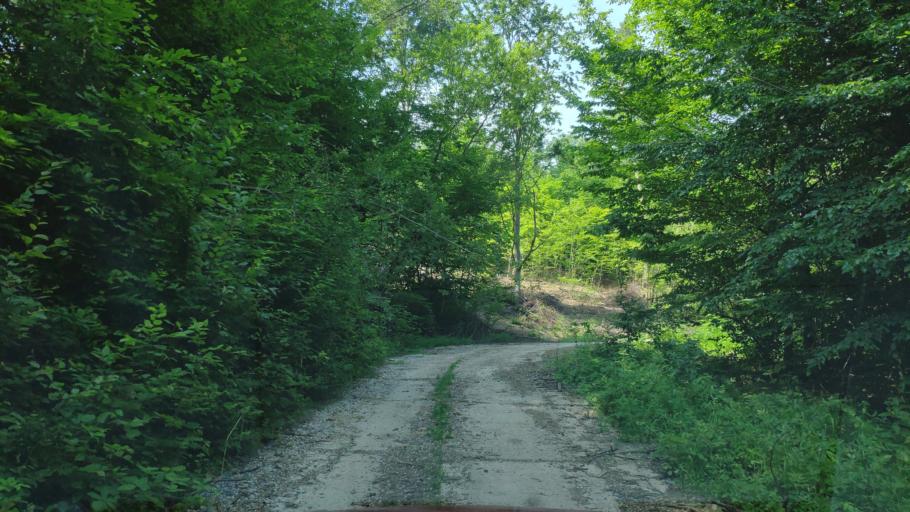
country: SK
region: Presovsky
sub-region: Okres Presov
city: Presov
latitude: 48.9720
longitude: 21.1470
